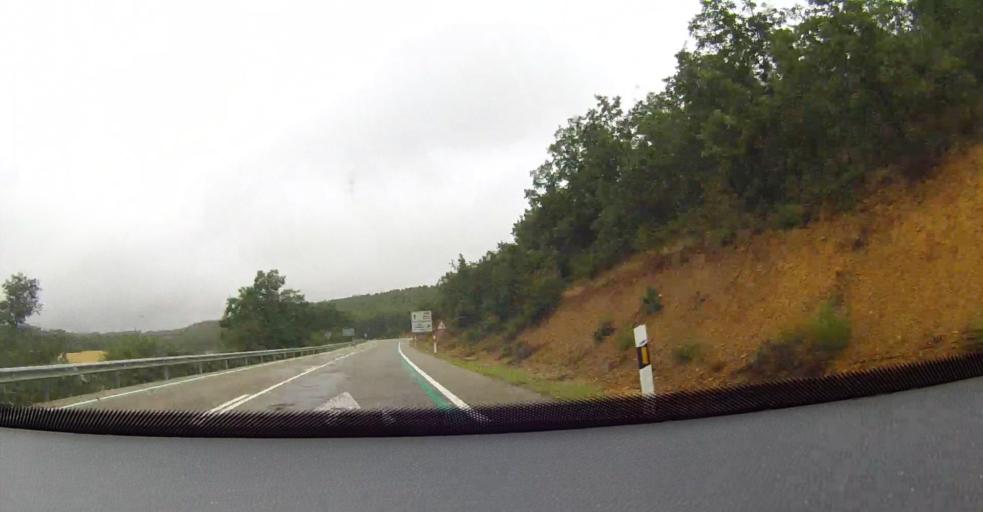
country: ES
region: Castille and Leon
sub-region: Provincia de Palencia
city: Saldana
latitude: 42.5467
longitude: -4.7334
